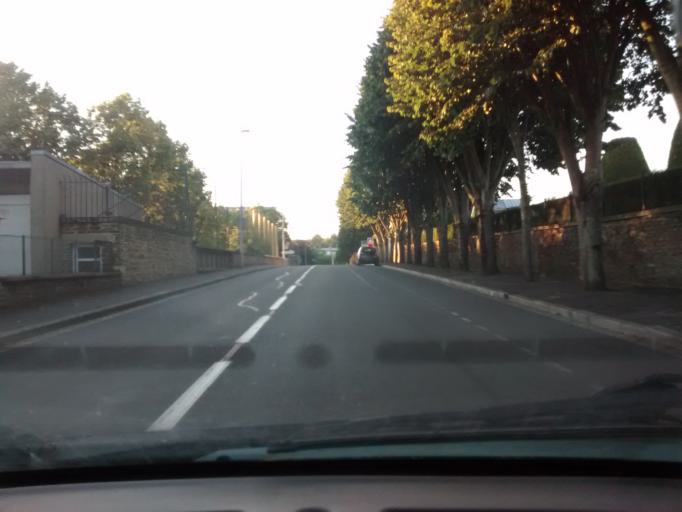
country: FR
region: Lower Normandy
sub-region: Departement de la Manche
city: Saint-Lo
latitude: 49.1164
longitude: -1.0831
